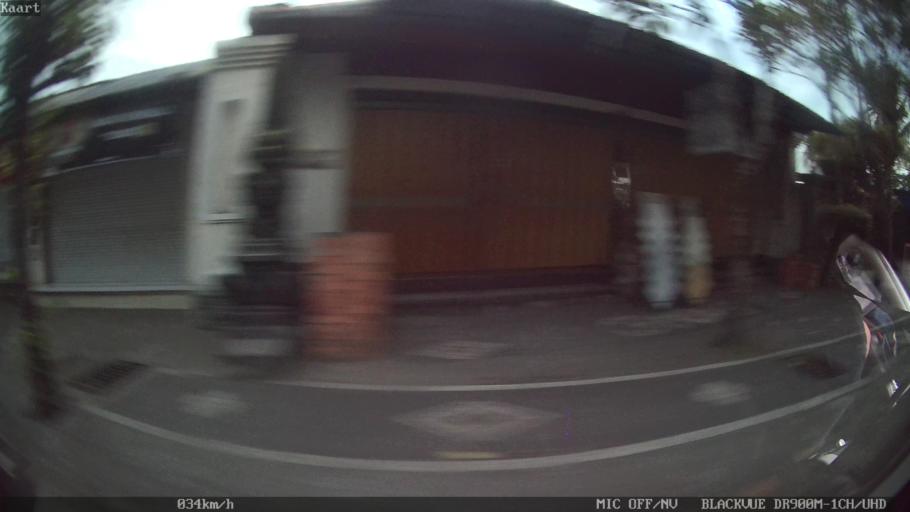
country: ID
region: Bali
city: Banjar Pasekan
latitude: -8.6381
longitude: 115.2825
